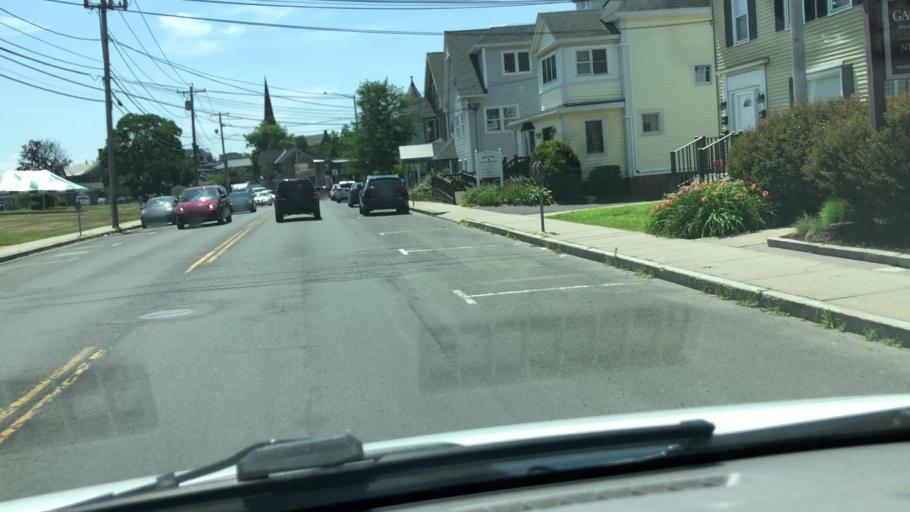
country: US
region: Massachusetts
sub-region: Hampshire County
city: Northampton
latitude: 42.3230
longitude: -72.6324
